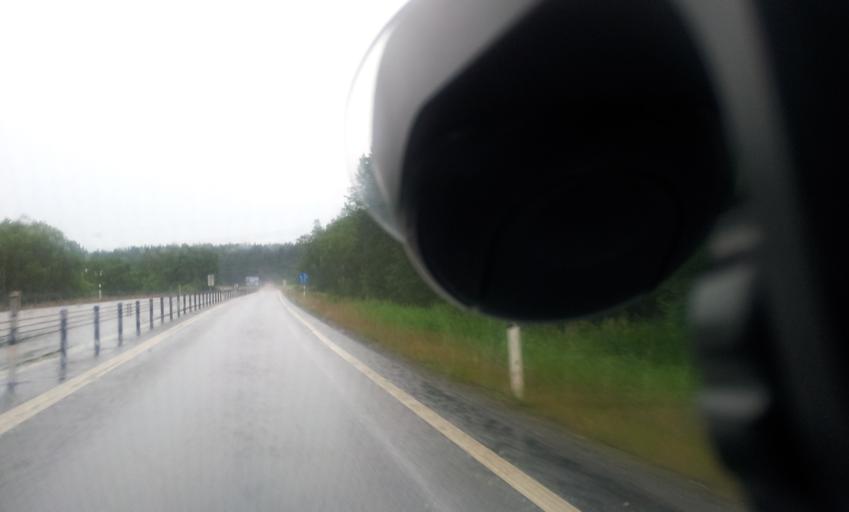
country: SE
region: OEstergoetland
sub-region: Valdemarsviks Kommun
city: Valdemarsvik
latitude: 58.1965
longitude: 16.5466
